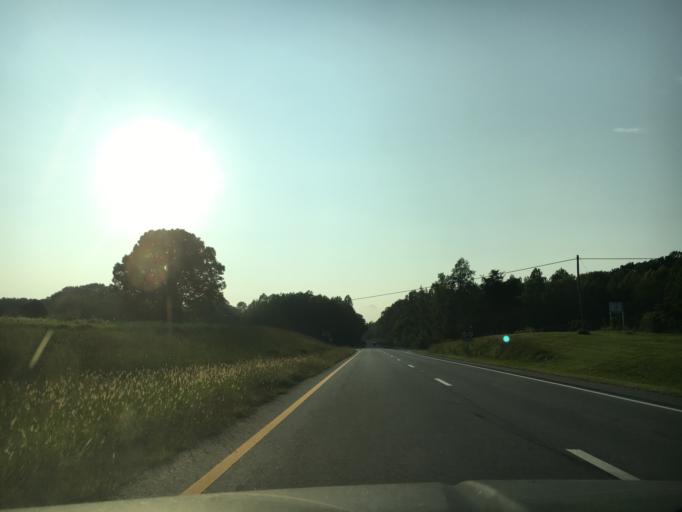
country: US
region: Virginia
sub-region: Appomattox County
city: Appomattox
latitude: 37.2736
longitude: -78.6788
